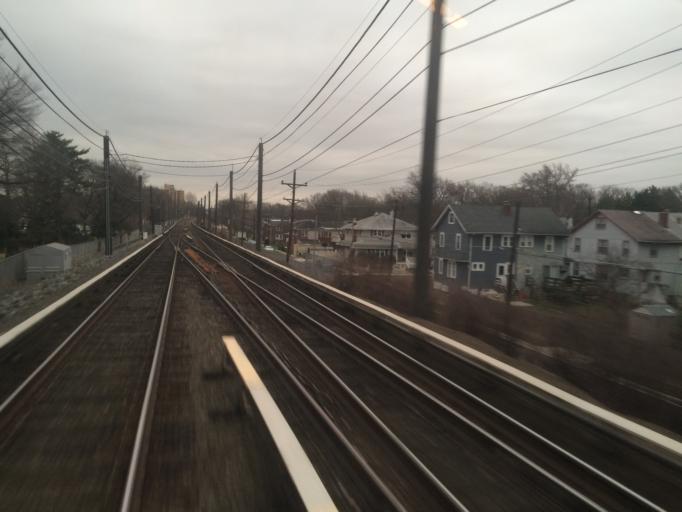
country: US
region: New Jersey
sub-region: Camden County
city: Collingswood
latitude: 39.9110
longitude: -75.0564
